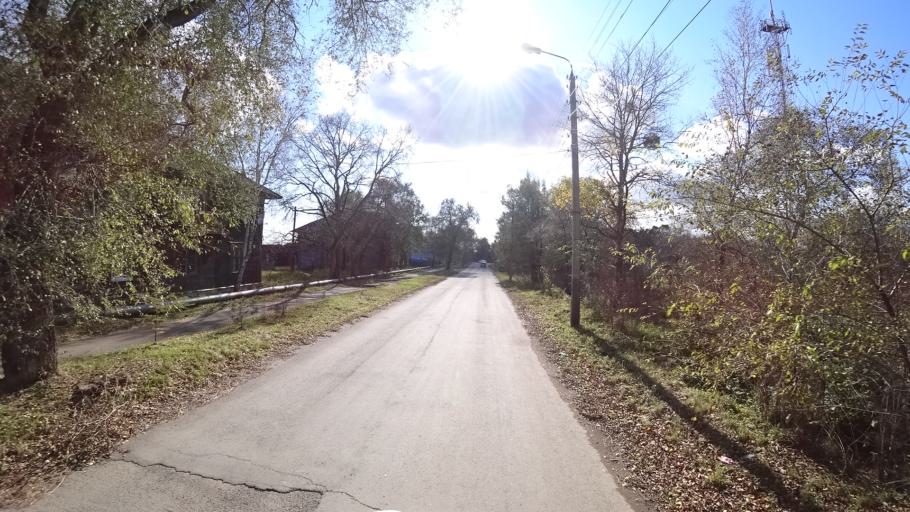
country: RU
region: Khabarovsk Krai
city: Amursk
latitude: 50.0970
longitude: 136.4981
